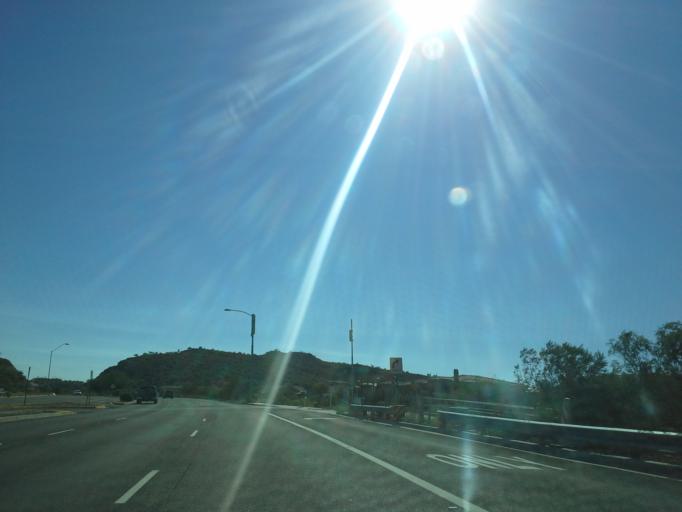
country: US
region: Arizona
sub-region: Maricopa County
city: Fountain Hills
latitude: 33.5786
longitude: -111.7754
